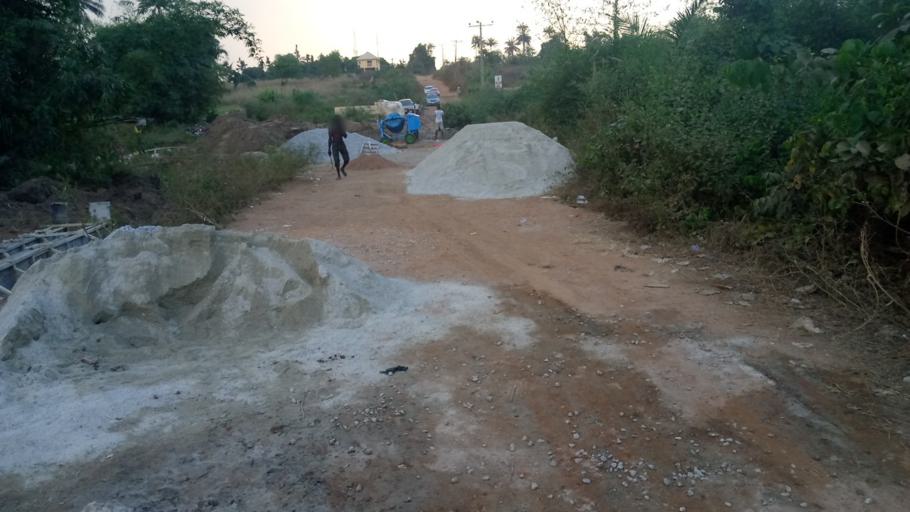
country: NG
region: Osun
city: Osogbo
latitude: 7.7660
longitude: 4.6114
